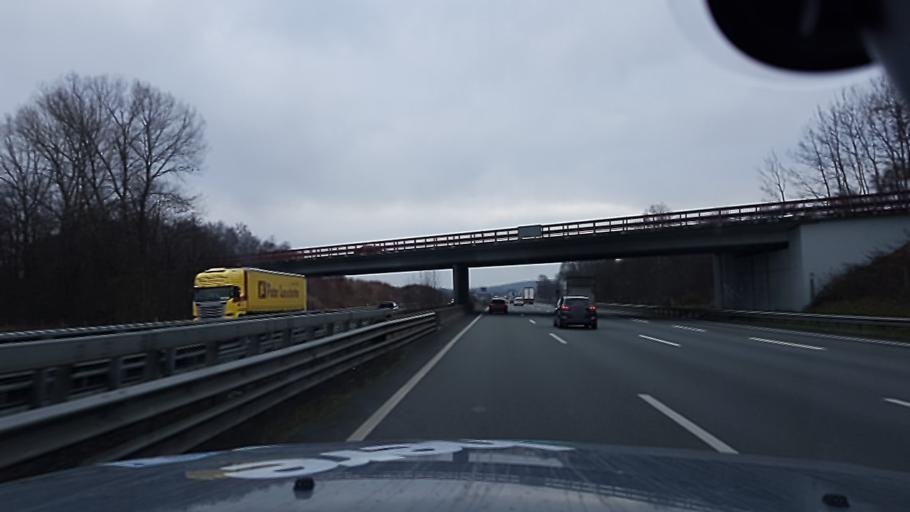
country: DE
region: Lower Saxony
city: Wallenhorst
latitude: 52.3954
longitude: 8.0378
